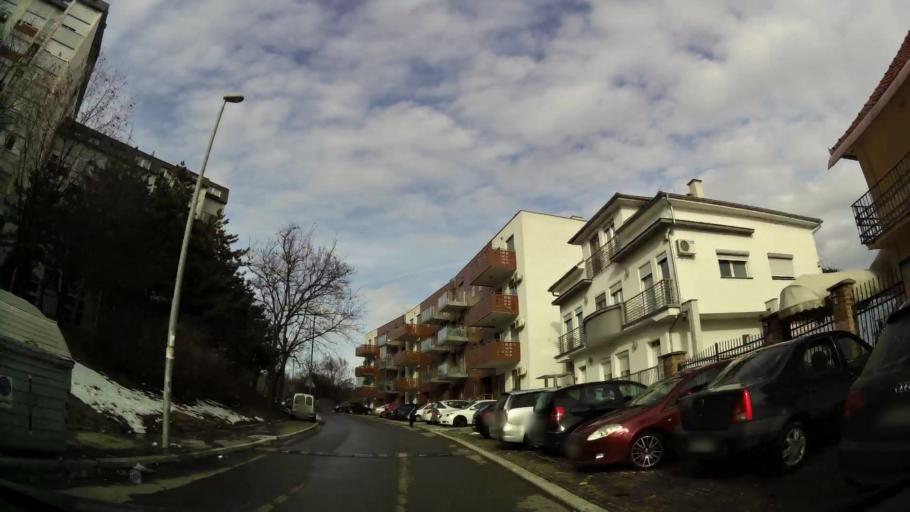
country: RS
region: Central Serbia
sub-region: Belgrade
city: Rakovica
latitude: 44.7516
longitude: 20.4386
